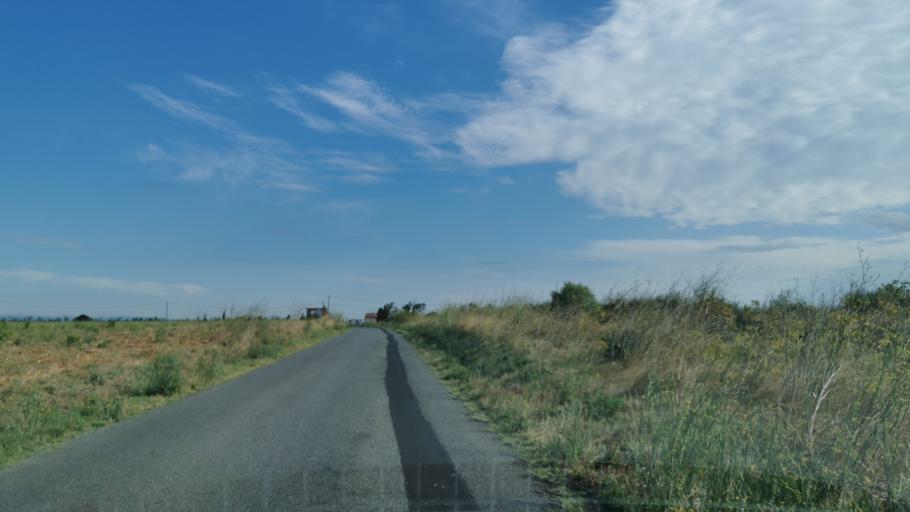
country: FR
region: Languedoc-Roussillon
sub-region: Departement de l'Aude
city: Narbonne
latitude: 43.1493
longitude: 3.0151
